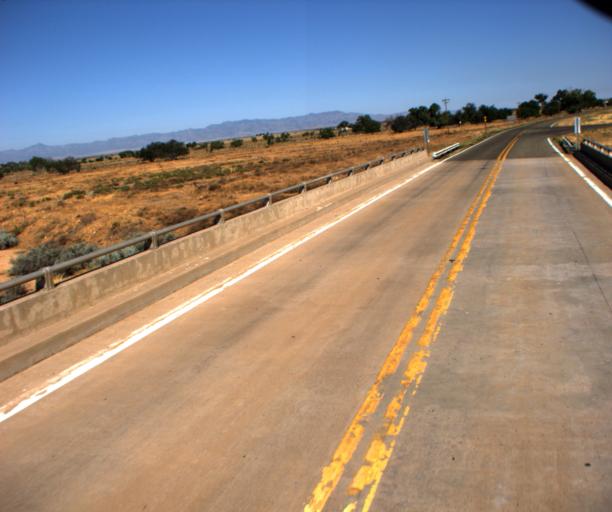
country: US
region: Arizona
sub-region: Graham County
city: Swift Trail Junction
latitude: 32.5839
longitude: -109.9598
